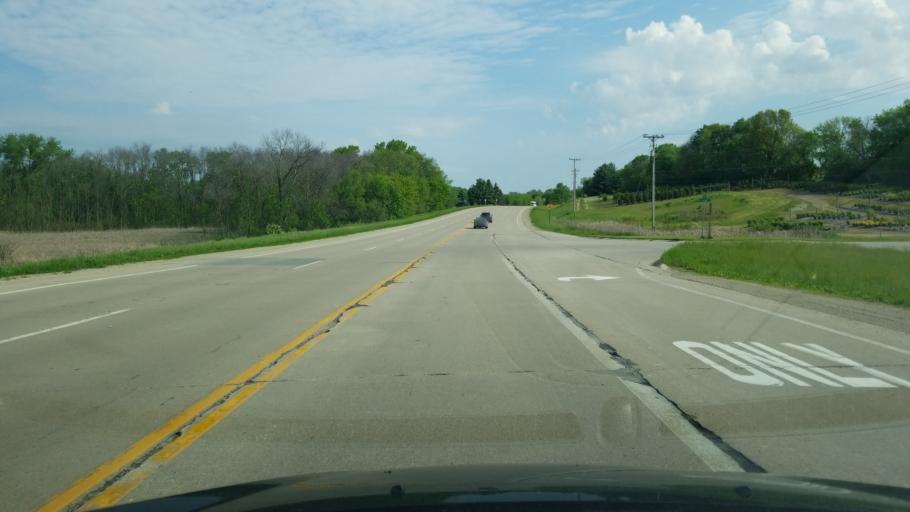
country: US
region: Wisconsin
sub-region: Dane County
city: McFarland
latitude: 43.0020
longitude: -89.3070
